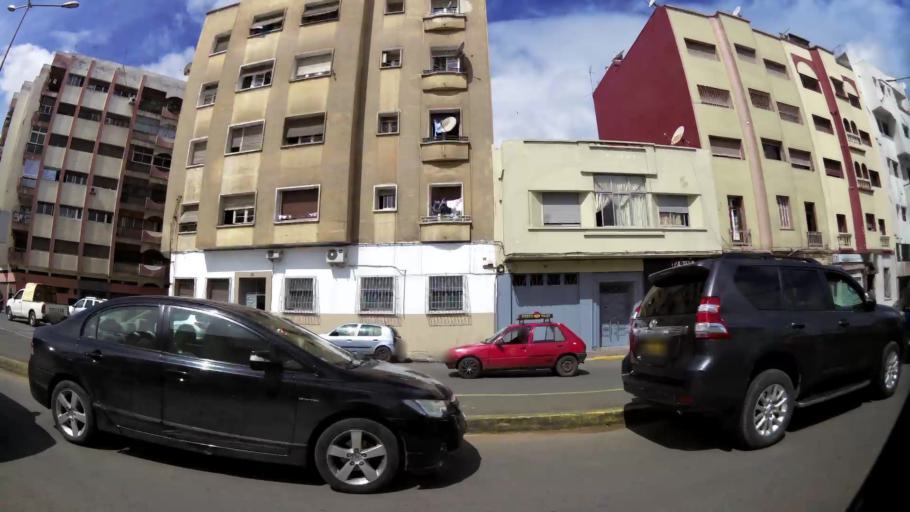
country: MA
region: Grand Casablanca
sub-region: Casablanca
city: Casablanca
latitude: 33.5937
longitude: -7.5936
